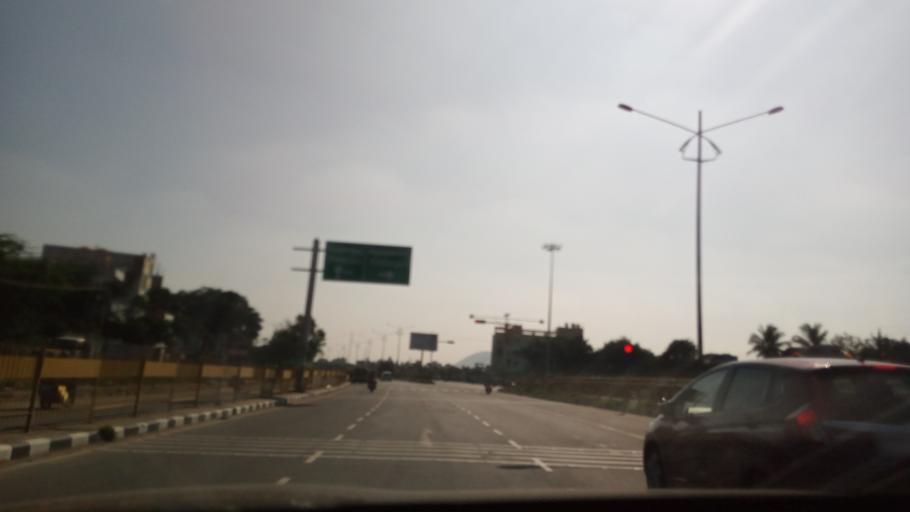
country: IN
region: Tamil Nadu
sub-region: Krishnagiri
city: Krishnagiri
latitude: 12.5244
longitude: 78.2324
